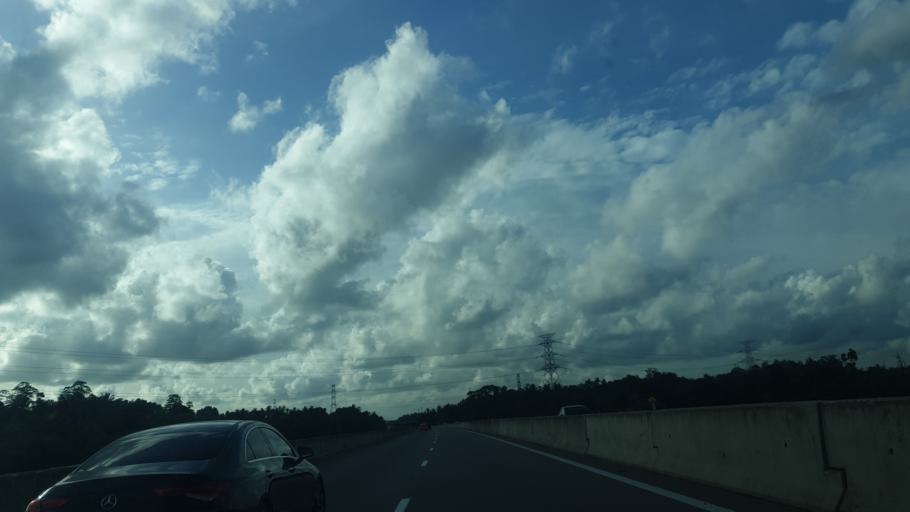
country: LK
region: Western
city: Kelaniya
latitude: 6.9632
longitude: 79.9750
